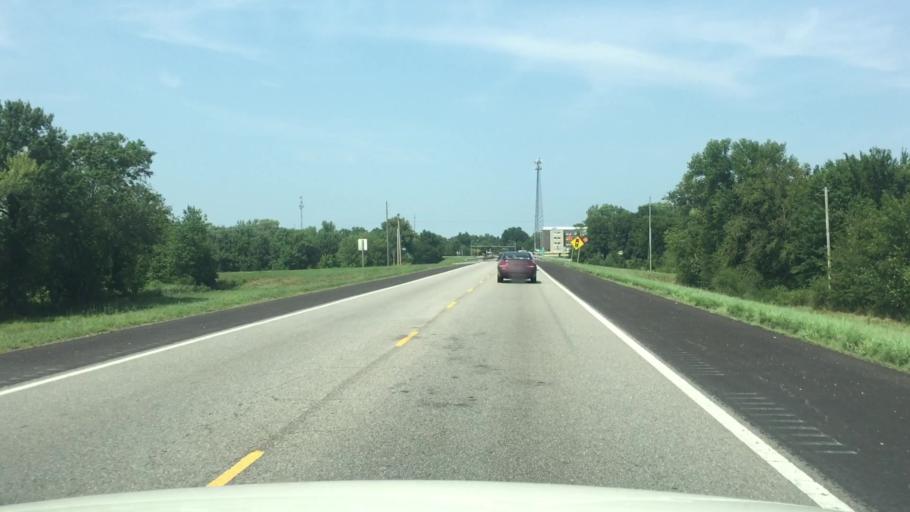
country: US
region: Kansas
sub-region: Crawford County
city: Pittsburg
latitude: 37.3774
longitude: -94.7076
